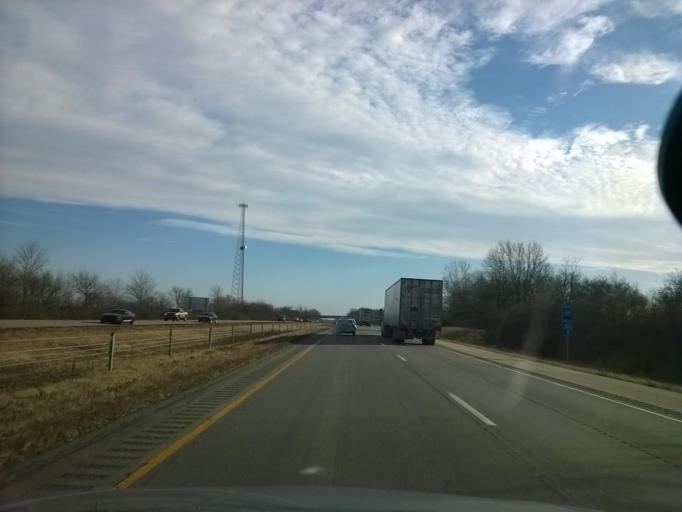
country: US
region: Indiana
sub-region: Johnson County
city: Franklin
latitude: 39.4590
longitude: -86.0013
